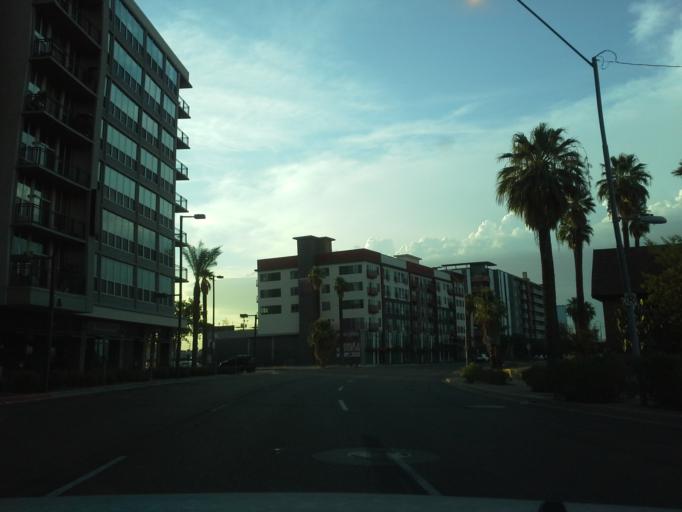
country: US
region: Arizona
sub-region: Maricopa County
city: Phoenix
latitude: 33.4550
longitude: -112.0683
